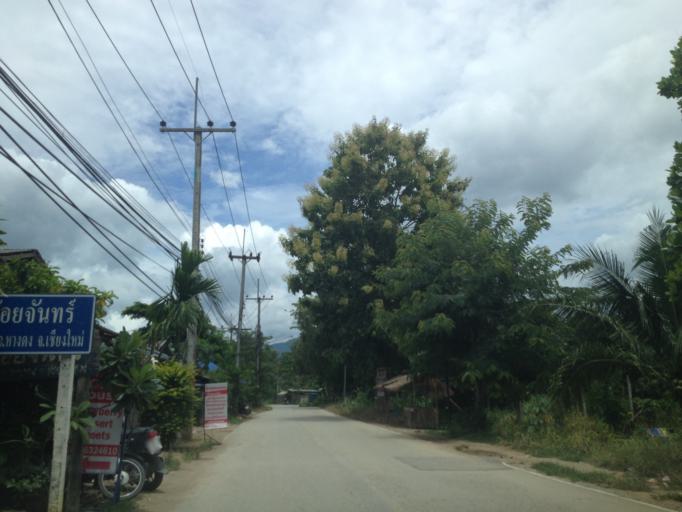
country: TH
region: Chiang Mai
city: Hang Dong
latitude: 18.7182
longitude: 98.9349
